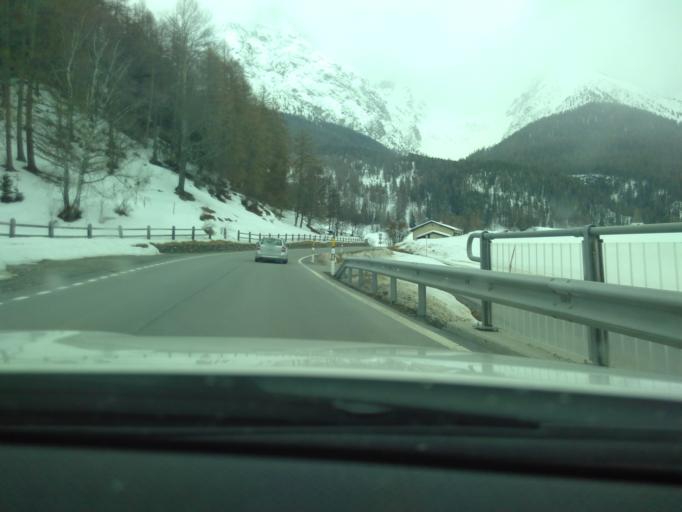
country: CH
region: Grisons
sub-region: Inn District
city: Scuol
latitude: 46.7802
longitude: 10.2590
